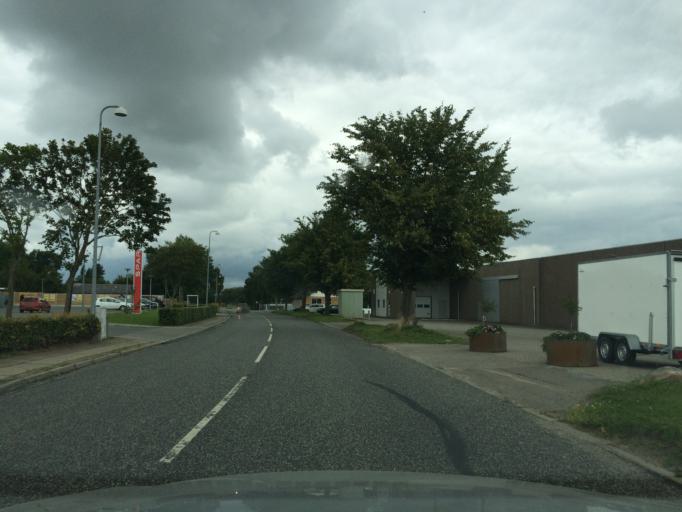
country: DK
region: Central Jutland
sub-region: Favrskov Kommune
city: Hammel
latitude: 56.2209
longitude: 9.7433
